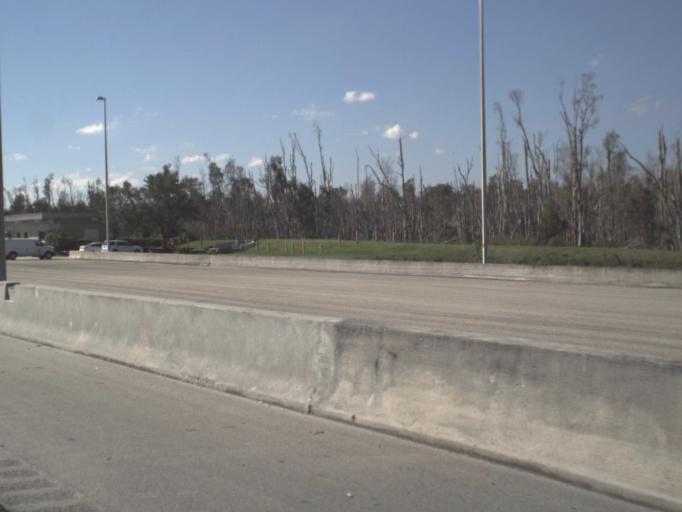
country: US
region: Florida
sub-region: Miami-Dade County
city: Doral
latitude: 25.8498
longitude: -80.3876
